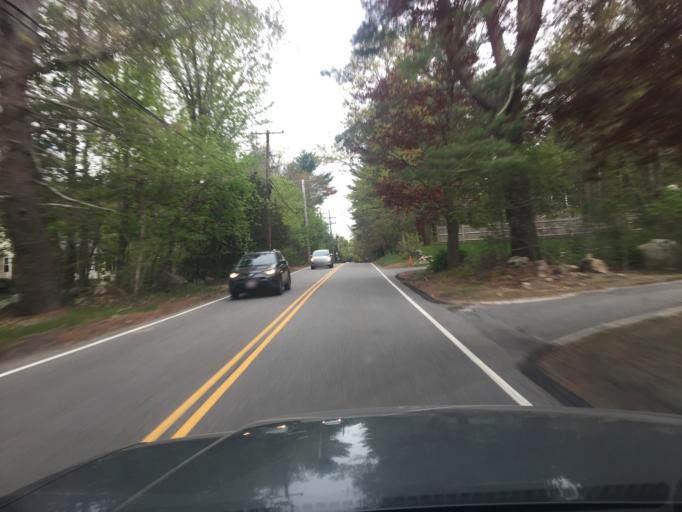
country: US
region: Massachusetts
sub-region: Norfolk County
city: Millis-Clicquot
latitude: 42.1701
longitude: -71.3445
